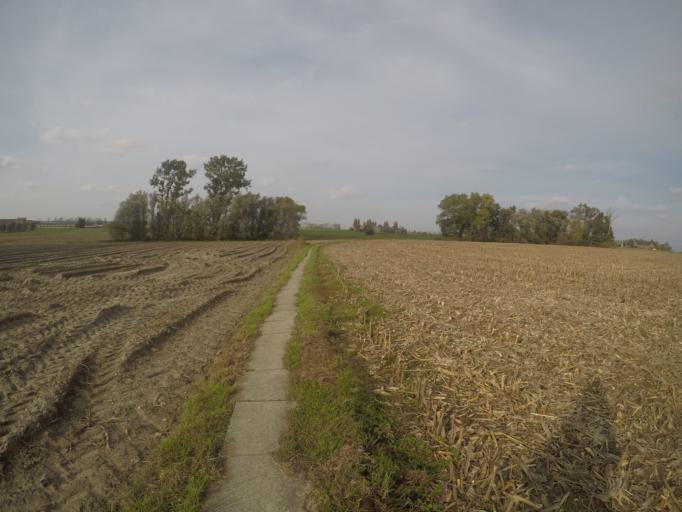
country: BE
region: Flanders
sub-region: Provincie West-Vlaanderen
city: Wervik
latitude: 50.8340
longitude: 3.0581
